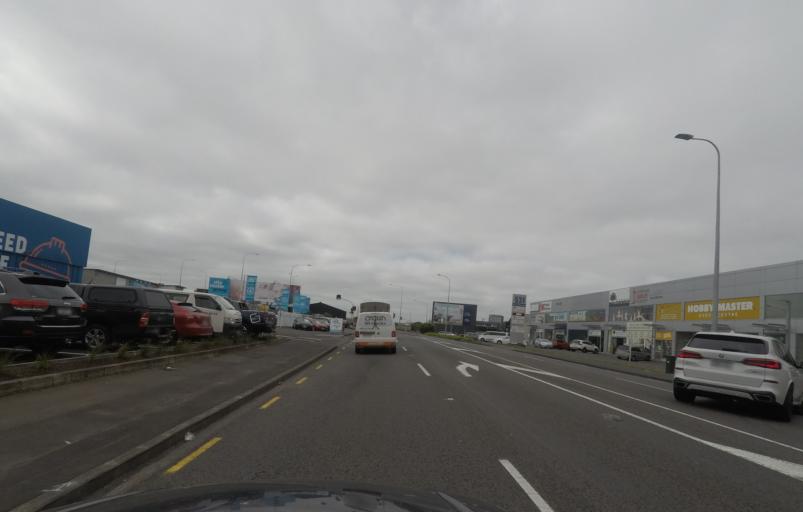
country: NZ
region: Auckland
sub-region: Auckland
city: Tamaki
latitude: -36.9072
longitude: 174.8119
